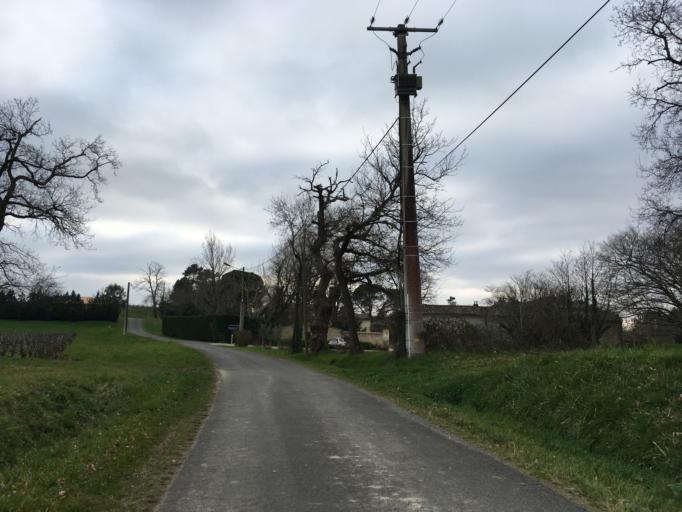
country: FR
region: Aquitaine
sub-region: Departement de la Gironde
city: Saint-Ciers-sur-Gironde
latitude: 45.3087
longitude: -0.6042
